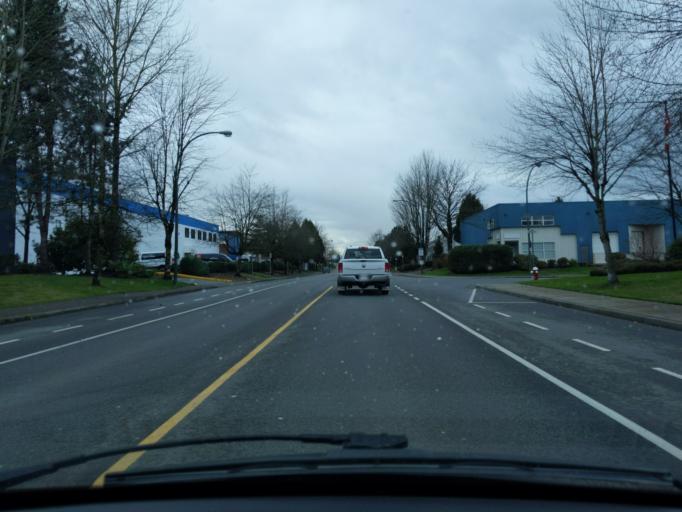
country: CA
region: British Columbia
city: Pitt Meadows
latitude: 49.2093
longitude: -122.6627
